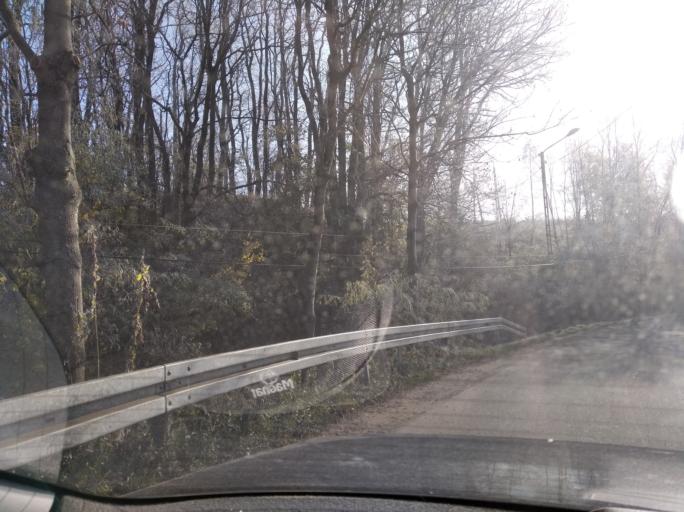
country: PL
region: Subcarpathian Voivodeship
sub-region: Powiat strzyzowski
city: Wysoka Strzyzowska
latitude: 49.8646
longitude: 21.7084
